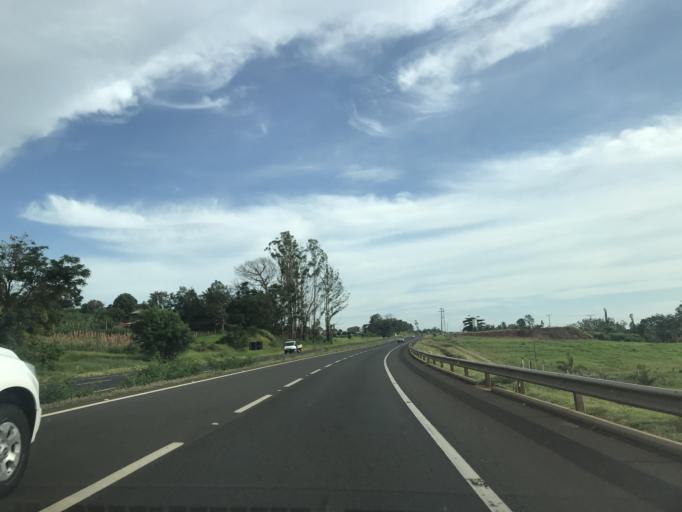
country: BR
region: Parana
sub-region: Mandaguacu
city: Mandaguacu
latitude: -23.3311
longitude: -52.1116
